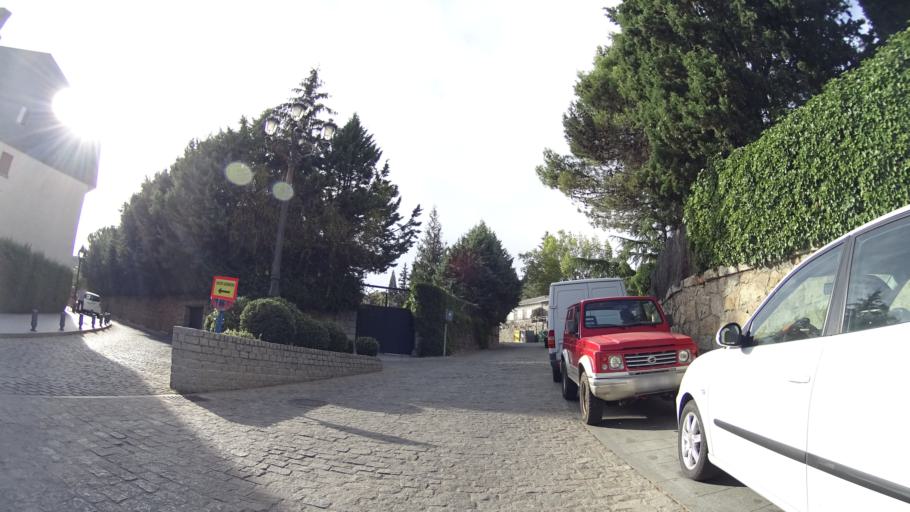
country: ES
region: Madrid
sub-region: Provincia de Madrid
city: Navacerrada
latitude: 40.7303
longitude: -4.0127
